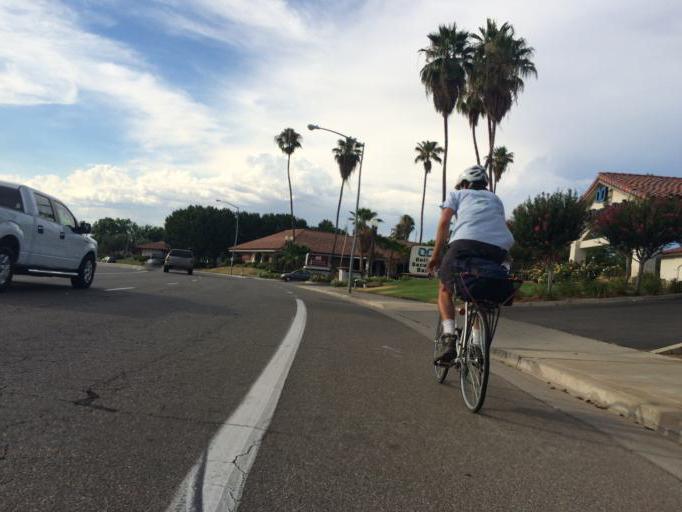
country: US
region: California
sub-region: Fresno County
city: Clovis
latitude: 36.8387
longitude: -119.7721
